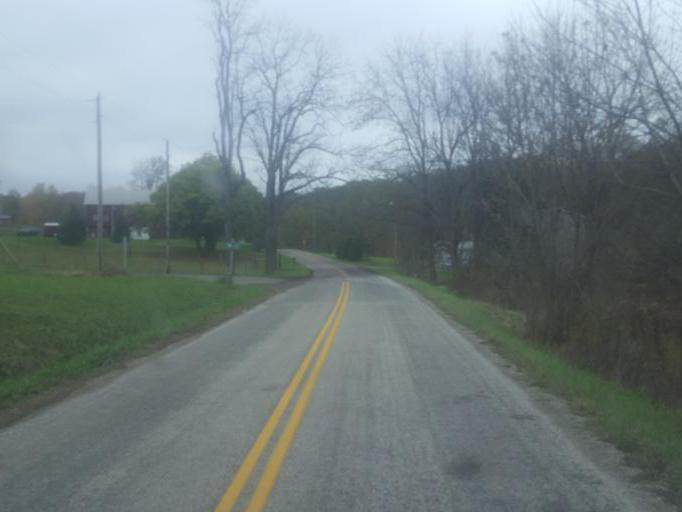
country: US
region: Ohio
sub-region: Ashland County
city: Loudonville
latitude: 40.7317
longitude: -82.3024
